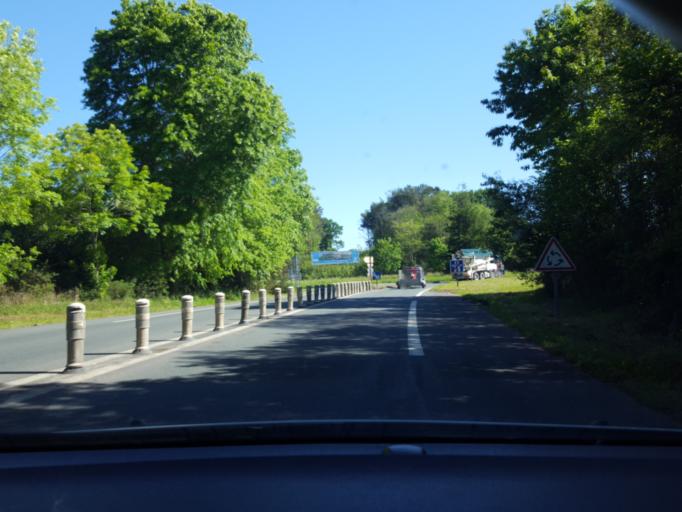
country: FR
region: Aquitaine
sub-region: Departement des Landes
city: Ondres
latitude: 43.5430
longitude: -1.4378
